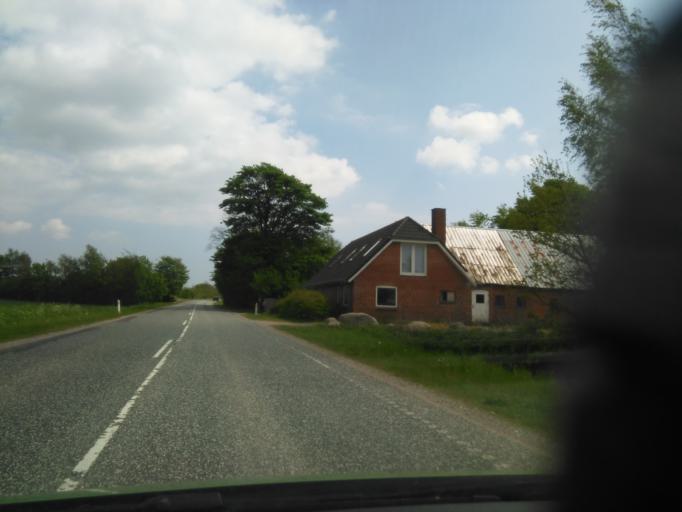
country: DK
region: Central Jutland
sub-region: Arhus Kommune
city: Solbjerg
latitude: 55.9851
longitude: 10.0374
